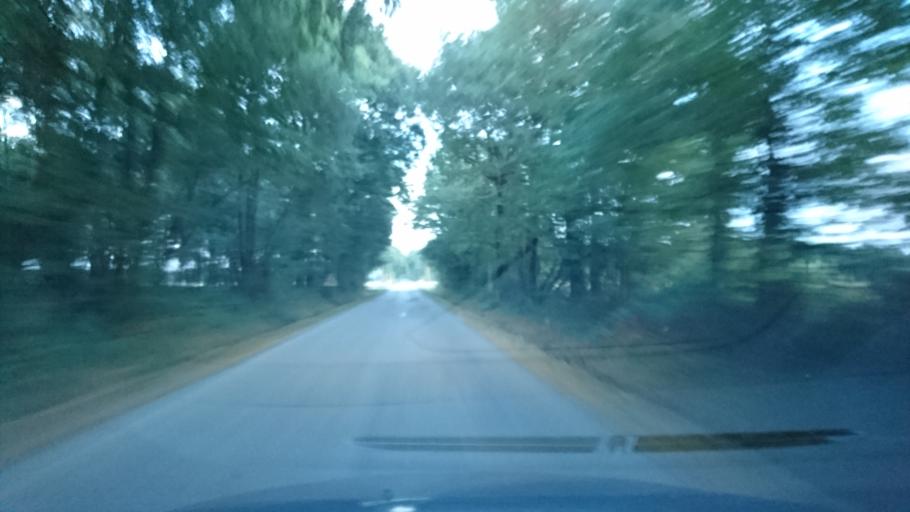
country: FR
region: Brittany
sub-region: Departement d'Ille-et-Vilaine
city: Pipriac
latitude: 47.8543
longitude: -1.9245
